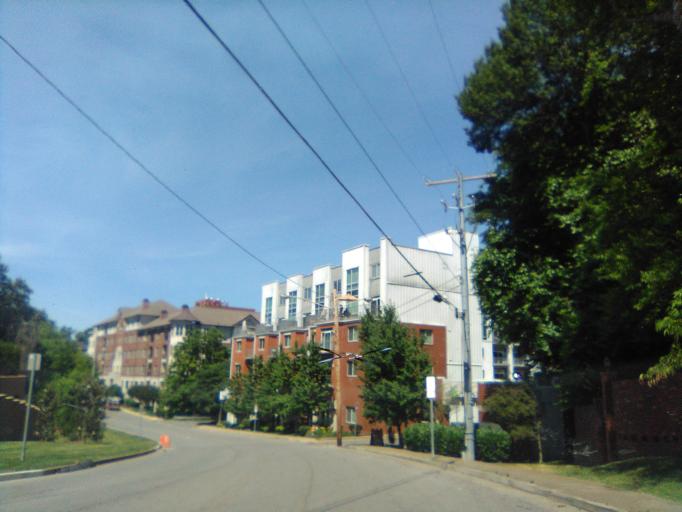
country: US
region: Tennessee
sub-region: Davidson County
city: Belle Meade
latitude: 36.1252
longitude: -86.8433
